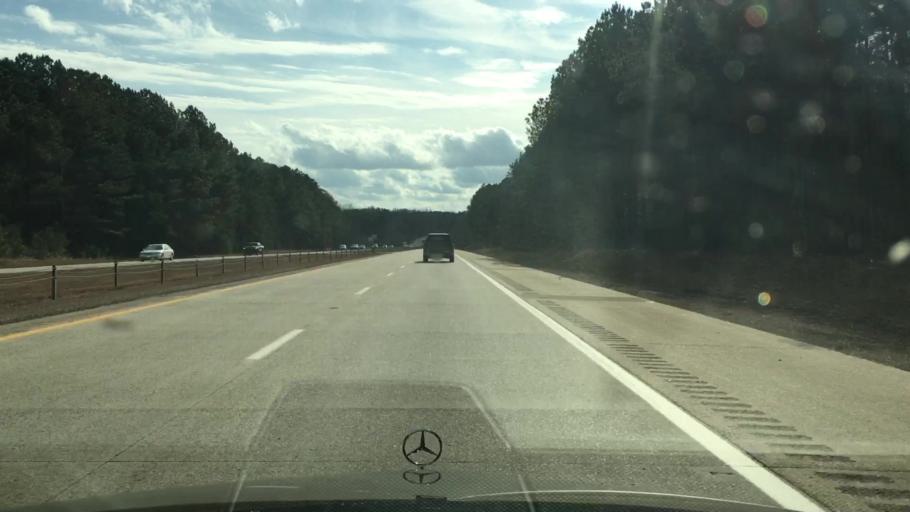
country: US
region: North Carolina
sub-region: Johnston County
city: Clayton
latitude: 35.5703
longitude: -78.5764
